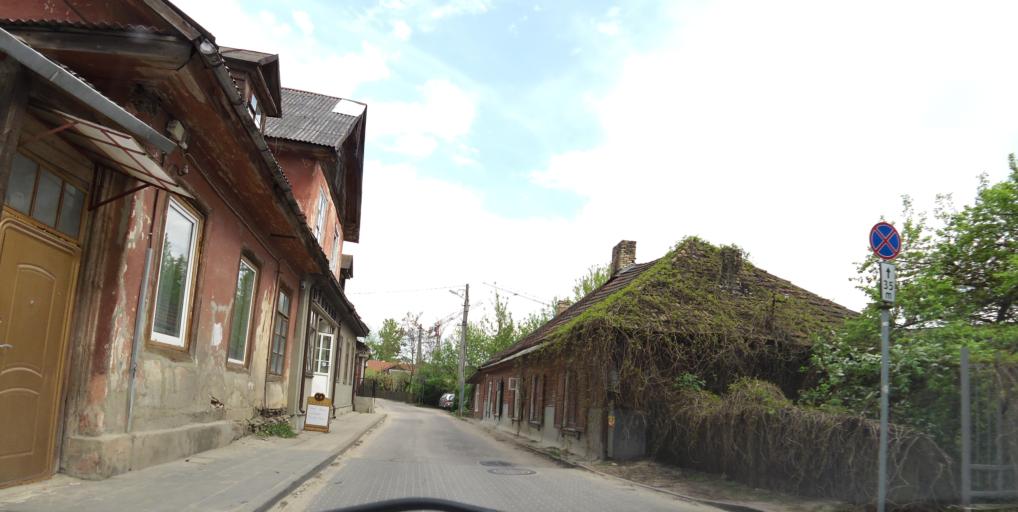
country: LT
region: Vilnius County
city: Rasos
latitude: 54.6821
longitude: 25.3023
